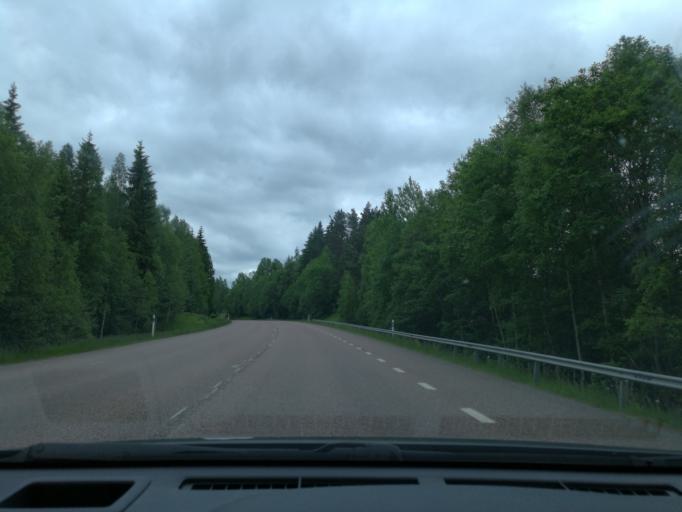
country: SE
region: Dalarna
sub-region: Ludvika Kommun
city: Ludvika
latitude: 60.1407
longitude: 15.3008
